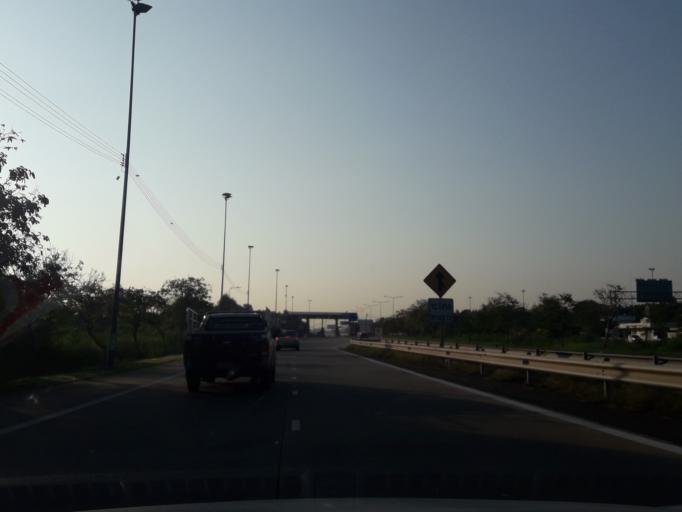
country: TH
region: Phra Nakhon Si Ayutthaya
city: Bang Pa-in
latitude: 14.1464
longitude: 100.5561
